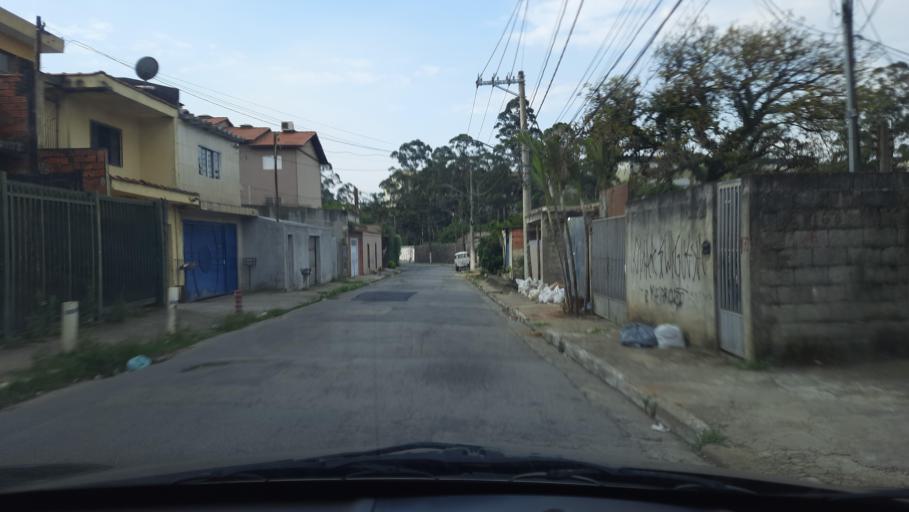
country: BR
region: Sao Paulo
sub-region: Caieiras
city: Caieiras
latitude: -23.4451
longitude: -46.7433
